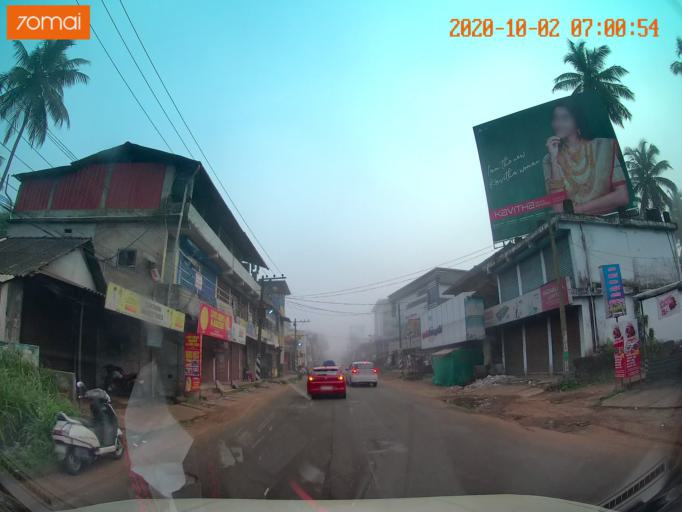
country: IN
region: Kerala
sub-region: Malappuram
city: Tirur
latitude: 10.8837
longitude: 76.0704
